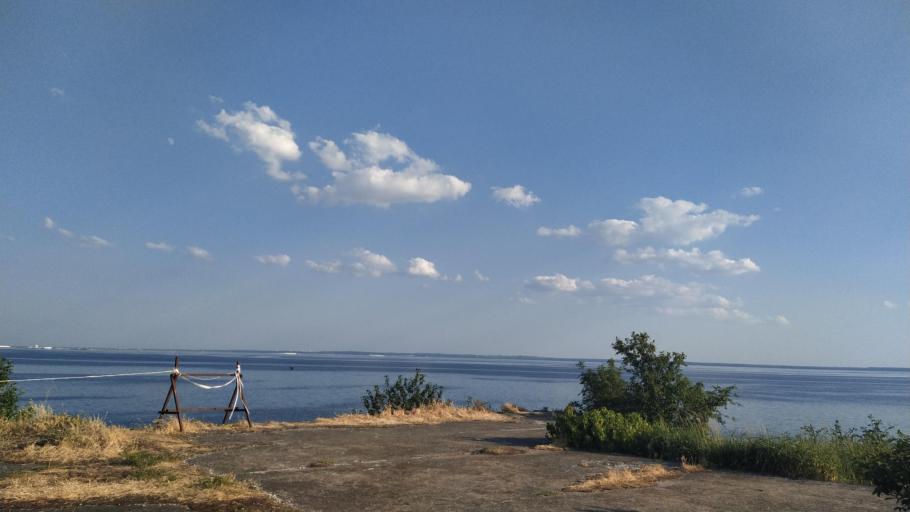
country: RU
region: St.-Petersburg
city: Bol'shaya Izhora
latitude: 60.0307
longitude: 29.6351
